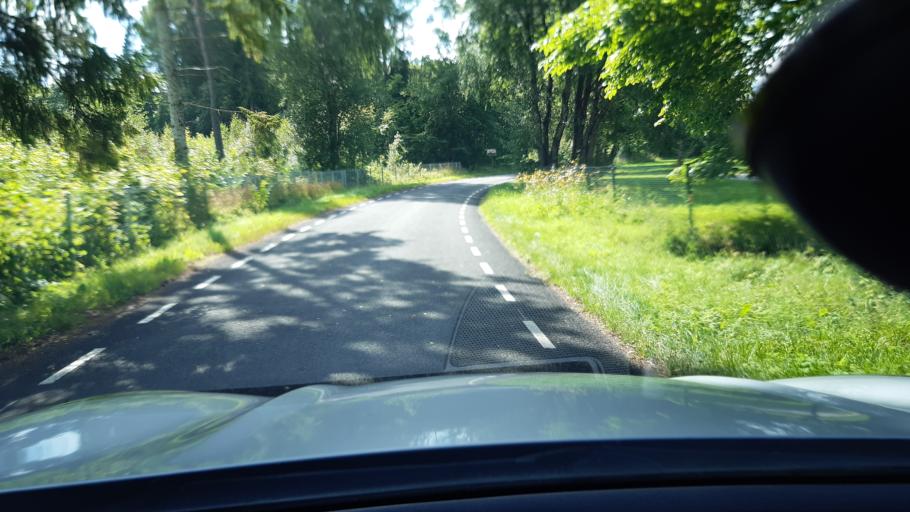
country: EE
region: Raplamaa
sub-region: Kehtna vald
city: Kehtna
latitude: 58.9394
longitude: 24.8977
